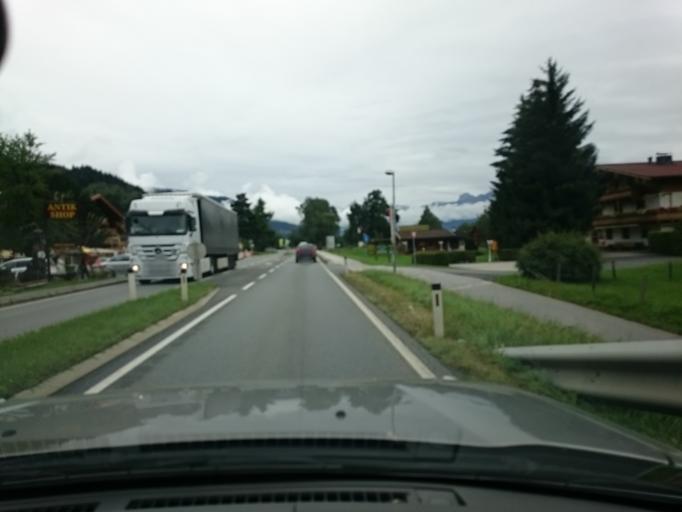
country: AT
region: Salzburg
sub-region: Politischer Bezirk Zell am See
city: Maishofen
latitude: 47.3568
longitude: 12.7999
